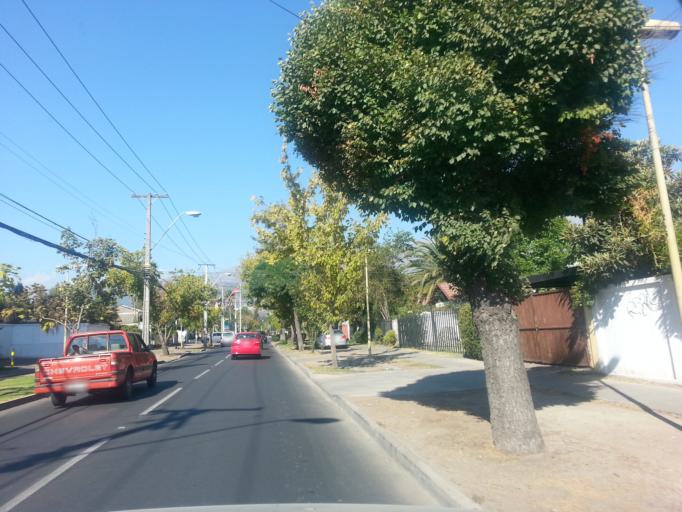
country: CL
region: Santiago Metropolitan
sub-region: Provincia de Santiago
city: Villa Presidente Frei, Nunoa, Santiago, Chile
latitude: -33.4255
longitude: -70.5662
